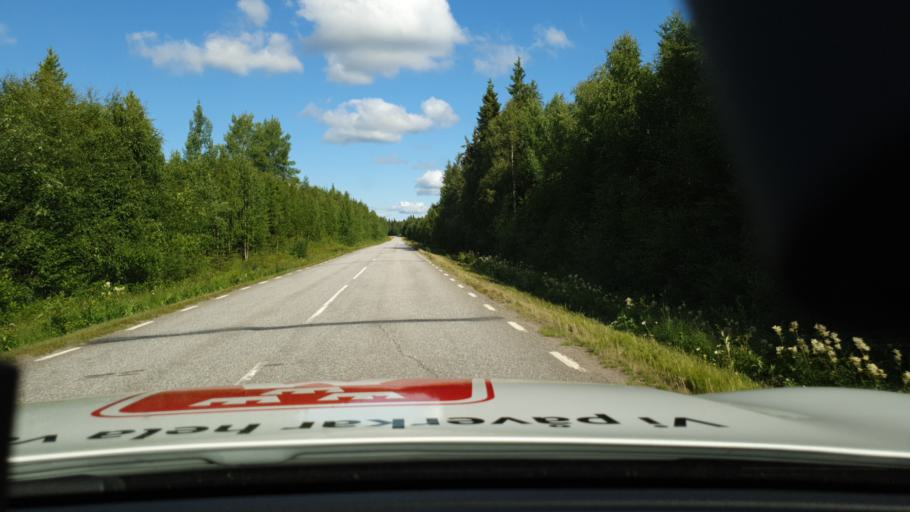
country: SE
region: Norrbotten
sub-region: Lulea Kommun
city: Ranea
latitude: 65.8667
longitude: 22.2299
